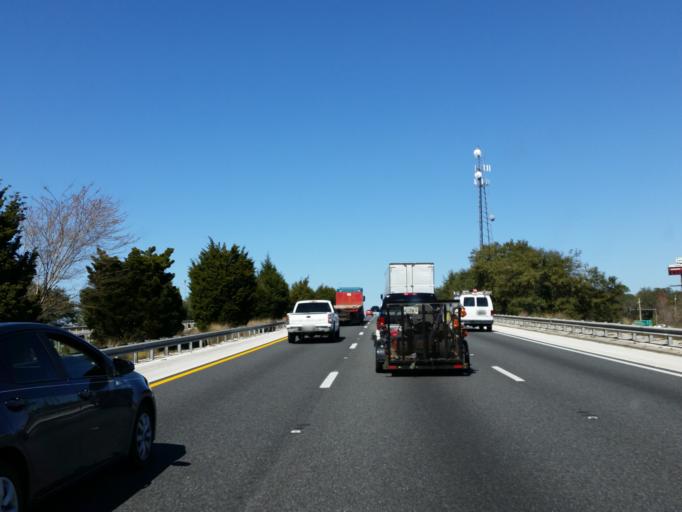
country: US
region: Florida
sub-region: Sumter County
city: Wildwood
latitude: 28.8712
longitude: -82.0921
